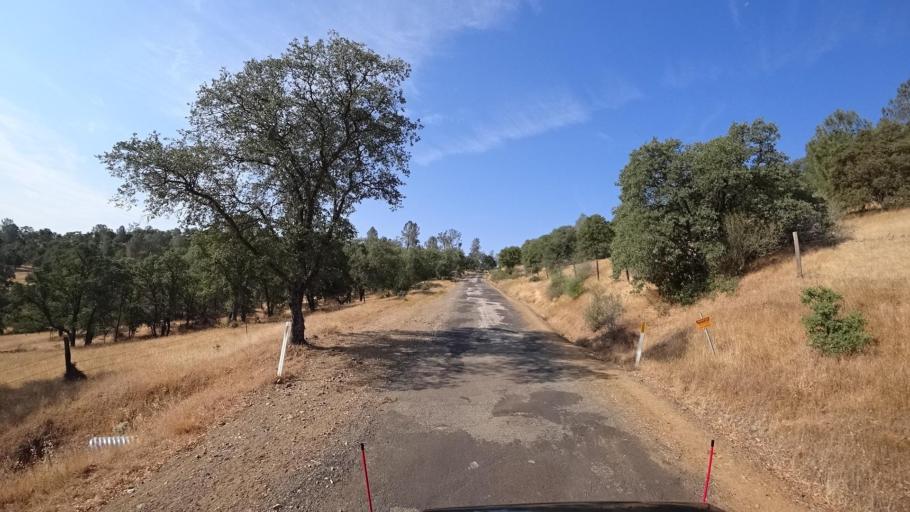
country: US
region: California
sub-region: Tuolumne County
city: Tuolumne City
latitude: 37.7288
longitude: -120.2458
